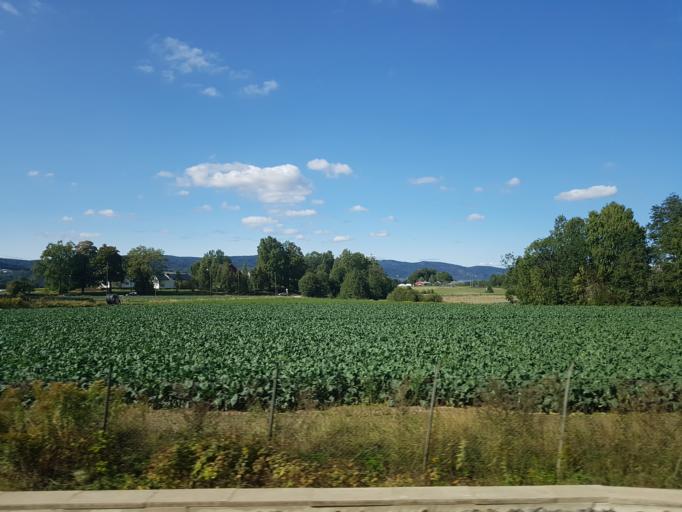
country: NO
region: Buskerud
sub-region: Lier
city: Lierbyen
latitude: 59.7592
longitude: 10.2770
